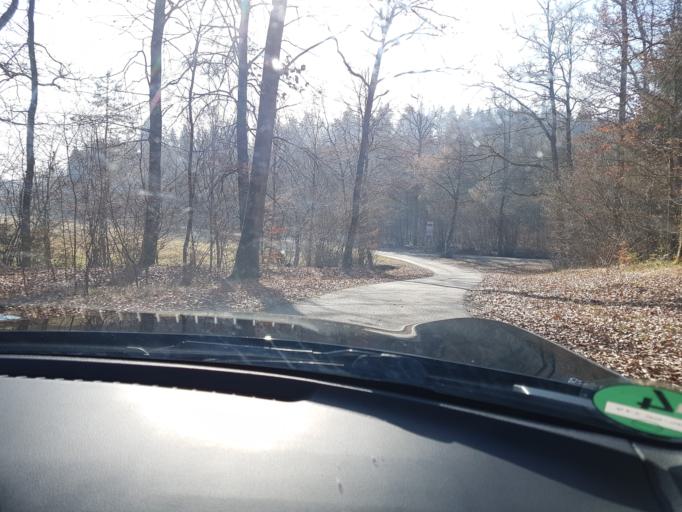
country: DE
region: Baden-Wuerttemberg
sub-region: Karlsruhe Region
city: Rosenberg
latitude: 49.4209
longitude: 9.4970
